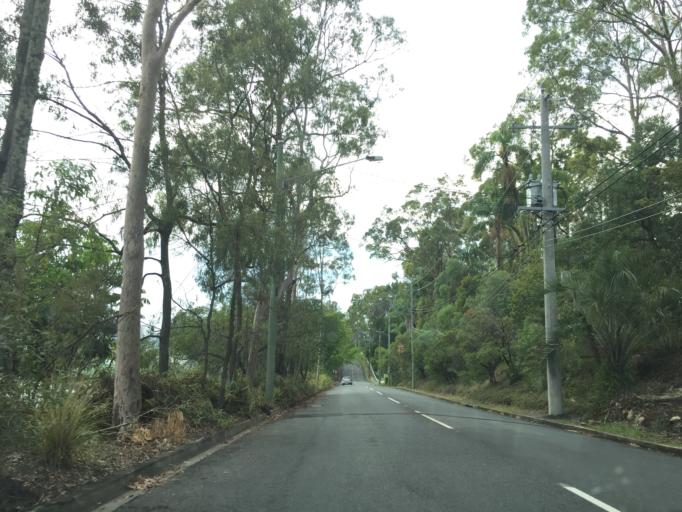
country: AU
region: Queensland
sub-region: Brisbane
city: Milton
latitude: -27.4608
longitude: 152.9887
